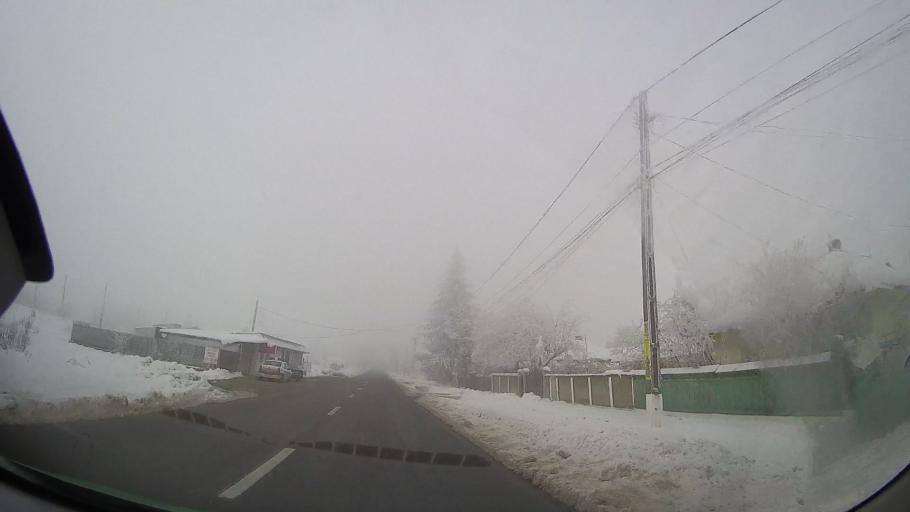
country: RO
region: Iasi
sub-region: Comuna Mircesti
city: Mircesti
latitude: 47.0920
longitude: 26.8215
